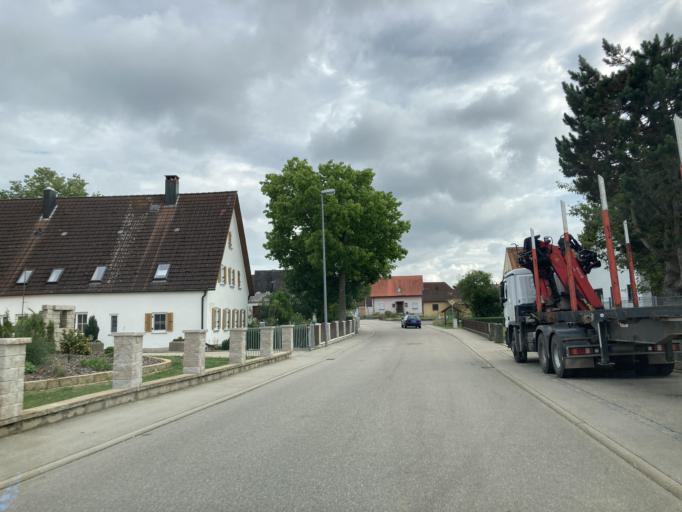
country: DE
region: Bavaria
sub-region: Swabia
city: Forheim
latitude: 48.7872
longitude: 10.4146
